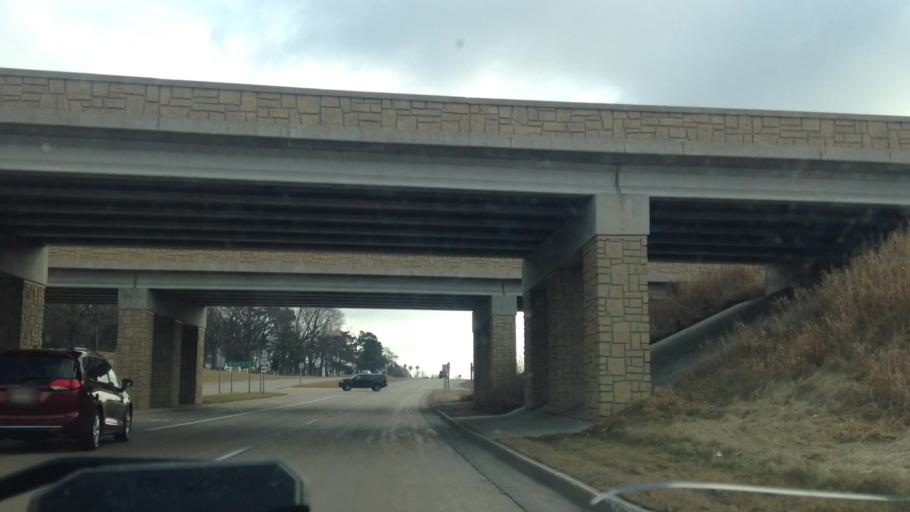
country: US
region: Wisconsin
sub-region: Dodge County
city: Beaver Dam
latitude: 43.4561
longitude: -88.8159
